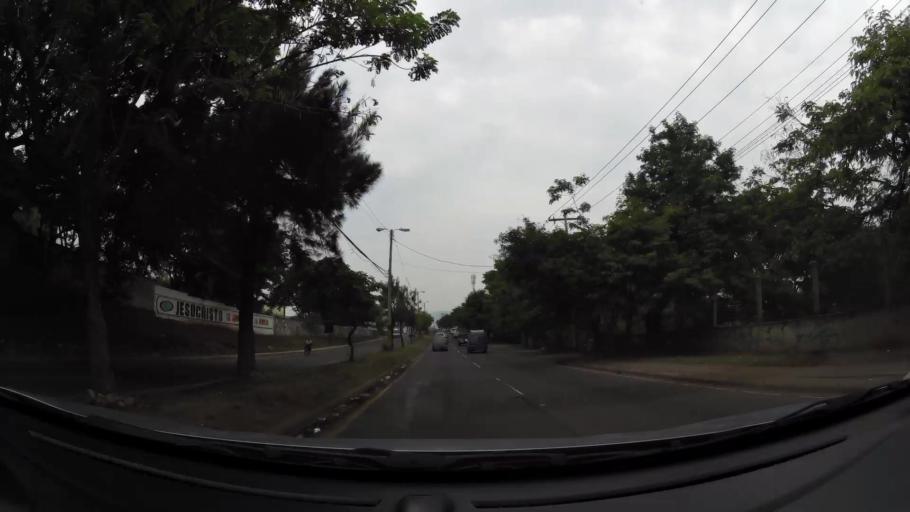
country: HN
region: Francisco Morazan
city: Tegucigalpa
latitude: 14.0753
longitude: -87.1917
